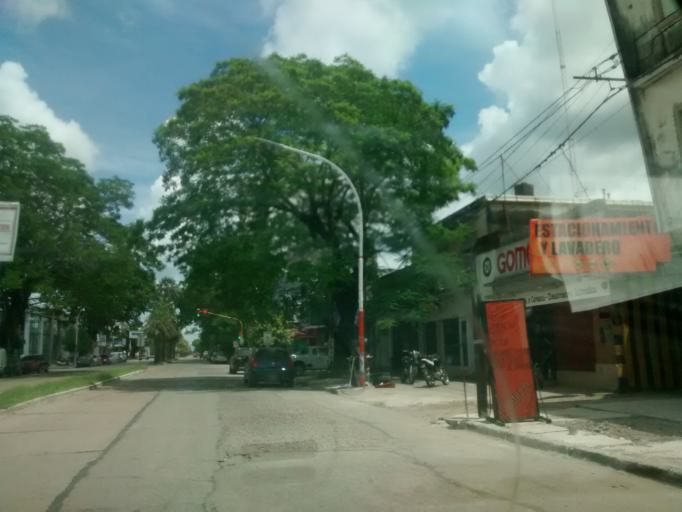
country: AR
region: Chaco
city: Resistencia
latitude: -27.4485
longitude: -58.9895
